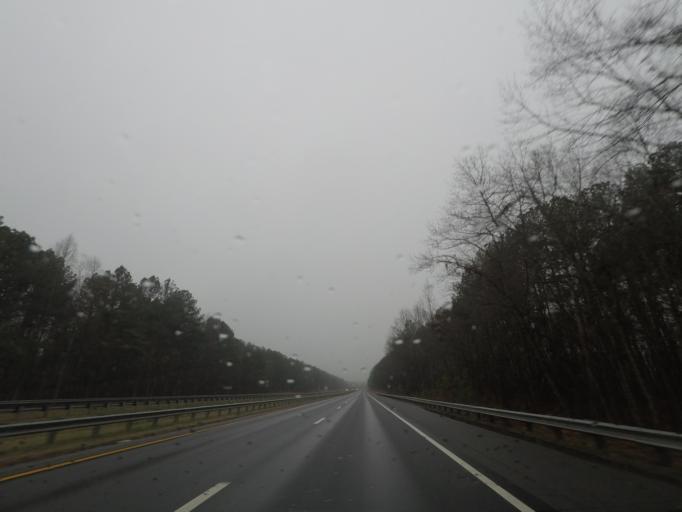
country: US
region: North Carolina
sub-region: Chatham County
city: Farmville
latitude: 35.5992
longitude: -79.1129
